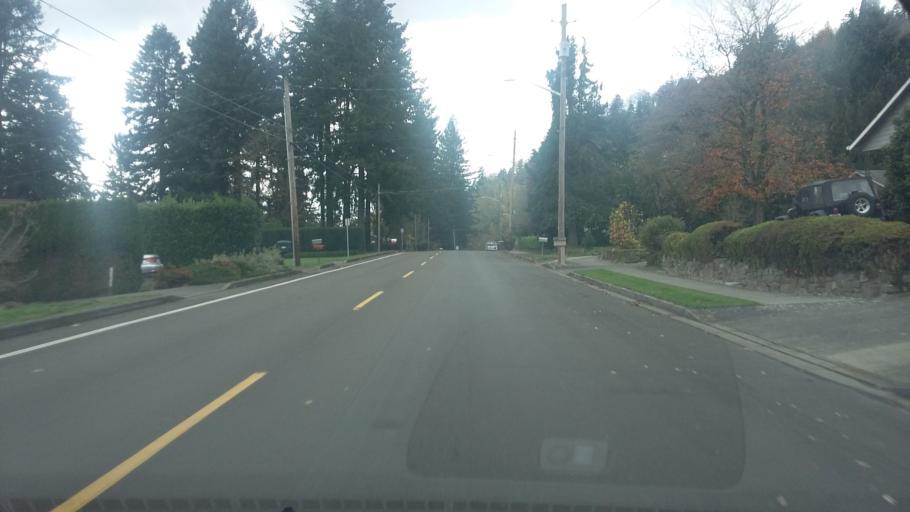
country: US
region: Washington
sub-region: Clark County
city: Camas
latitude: 45.5786
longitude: -122.4366
